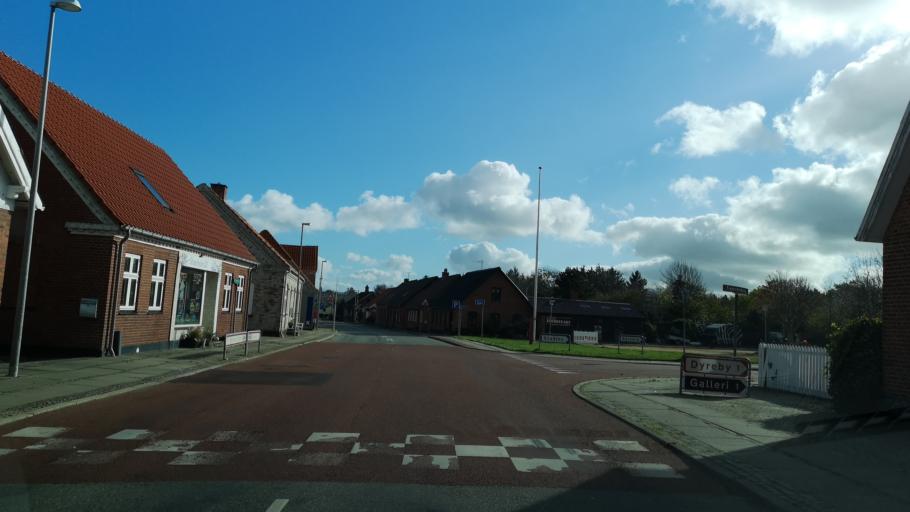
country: DK
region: South Denmark
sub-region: Varde Kommune
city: Oksbol
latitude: 55.7110
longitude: 8.3020
